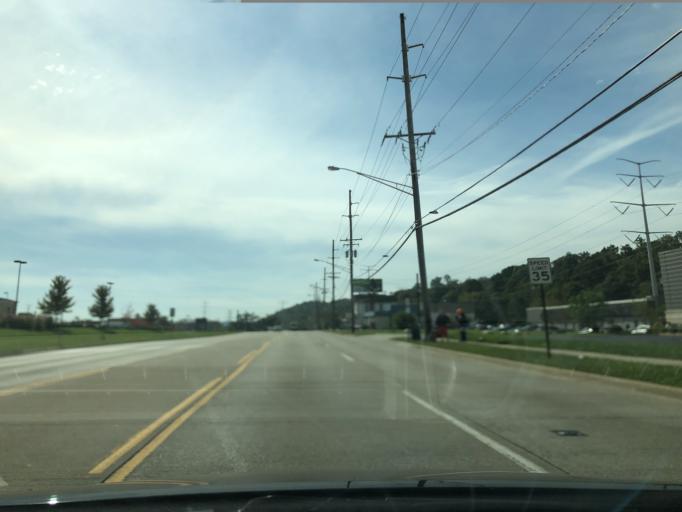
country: US
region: Ohio
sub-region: Hamilton County
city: Fairfax
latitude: 39.1492
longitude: -84.4045
